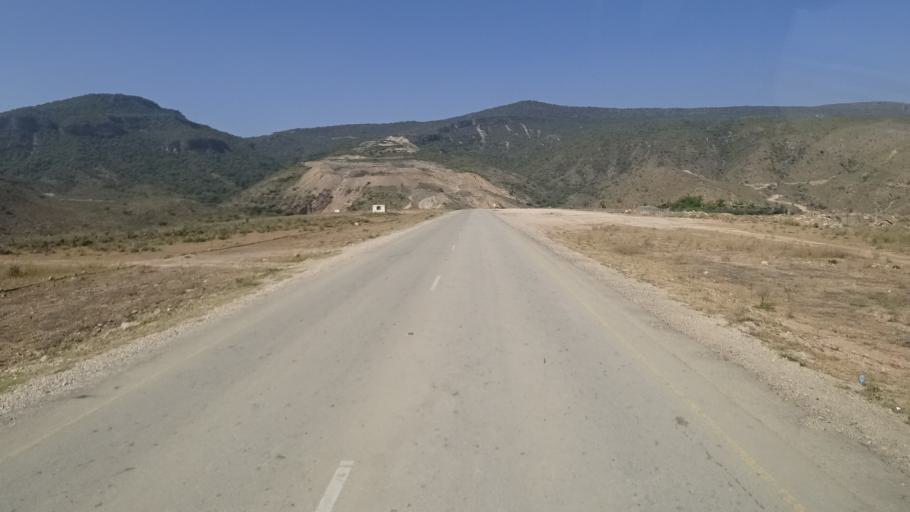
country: OM
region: Zufar
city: Salalah
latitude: 17.0374
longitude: 54.6129
